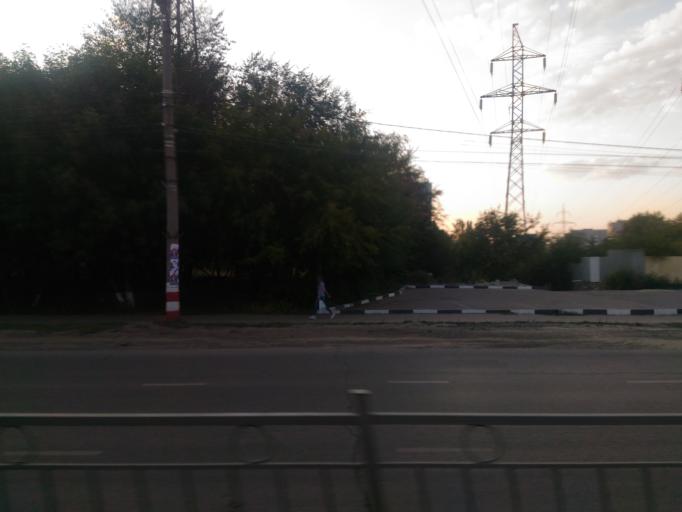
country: RU
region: Ulyanovsk
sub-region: Ulyanovskiy Rayon
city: Ulyanovsk
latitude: 54.2845
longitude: 48.3009
